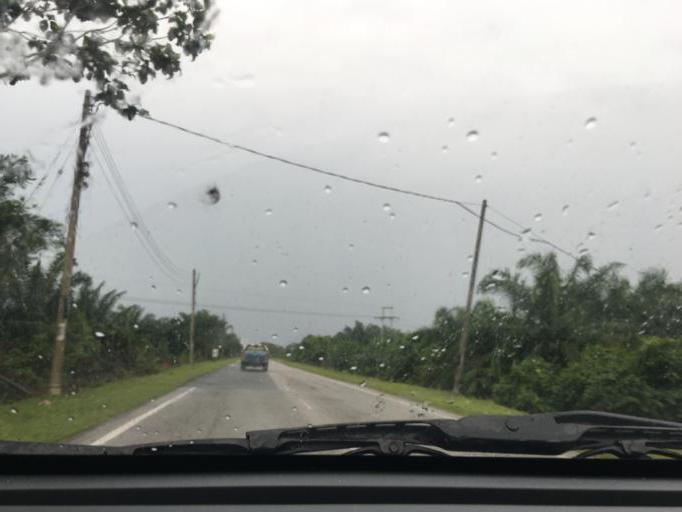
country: MY
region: Kedah
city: Sungai Petani
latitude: 5.6155
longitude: 100.6391
